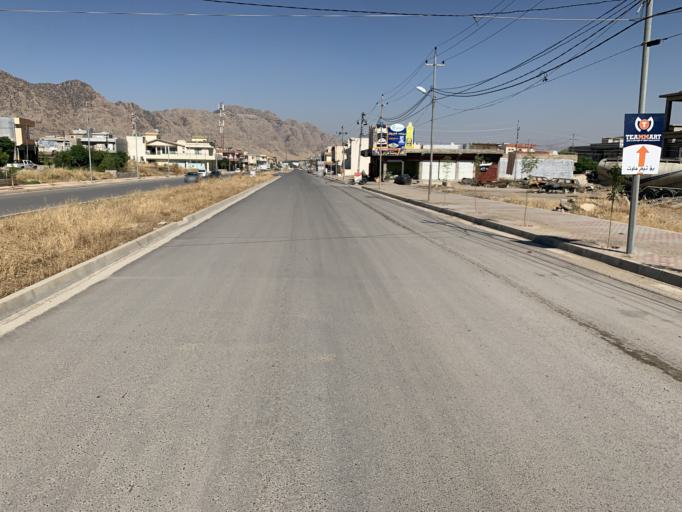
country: IQ
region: As Sulaymaniyah
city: Raniye
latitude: 36.2595
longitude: 44.8624
